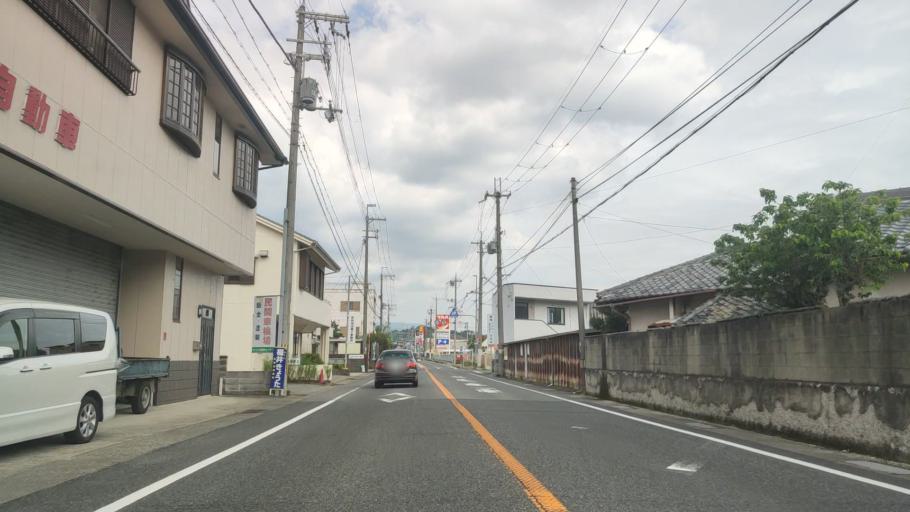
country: JP
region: Wakayama
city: Hashimoto
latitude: 34.2997
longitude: 135.5256
